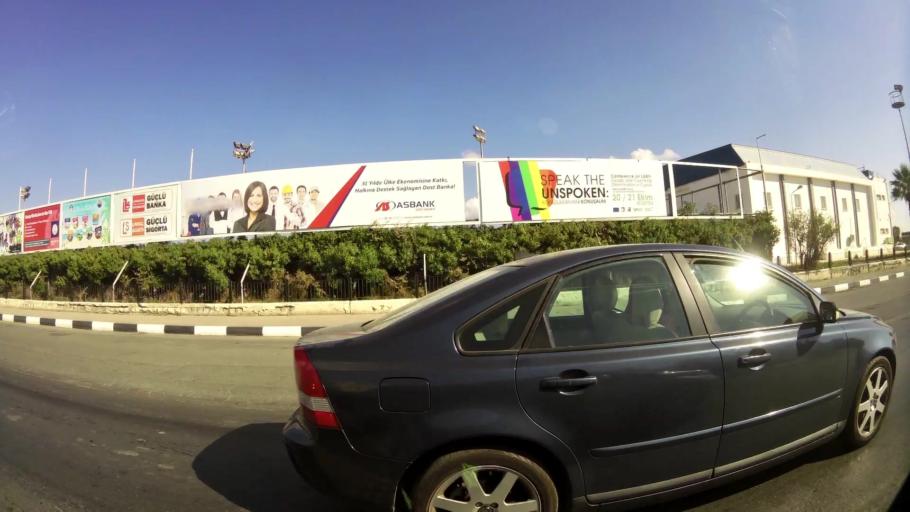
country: CY
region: Lefkosia
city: Nicosia
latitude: 35.2121
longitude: 33.3353
